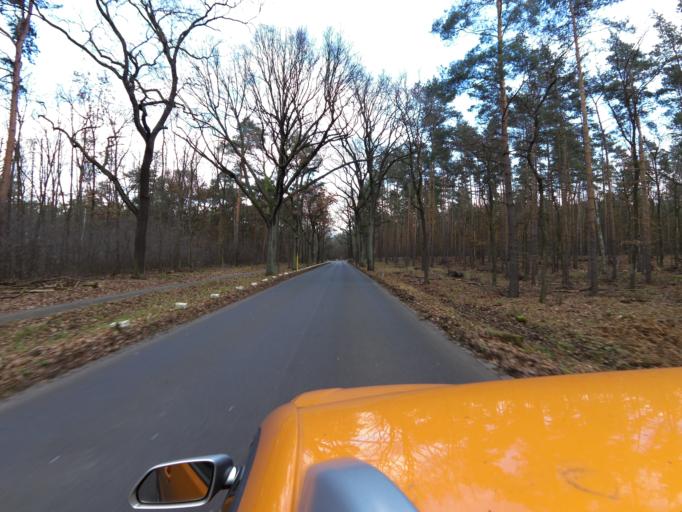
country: DE
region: Berlin
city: Gatow
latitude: 52.4877
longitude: 13.2032
